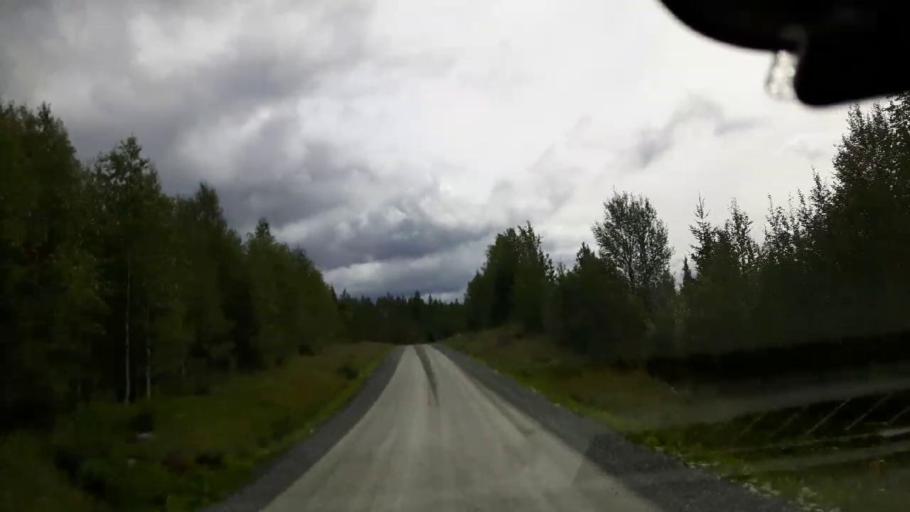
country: SE
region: Jaemtland
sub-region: Krokoms Kommun
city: Valla
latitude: 63.6026
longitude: 14.1336
